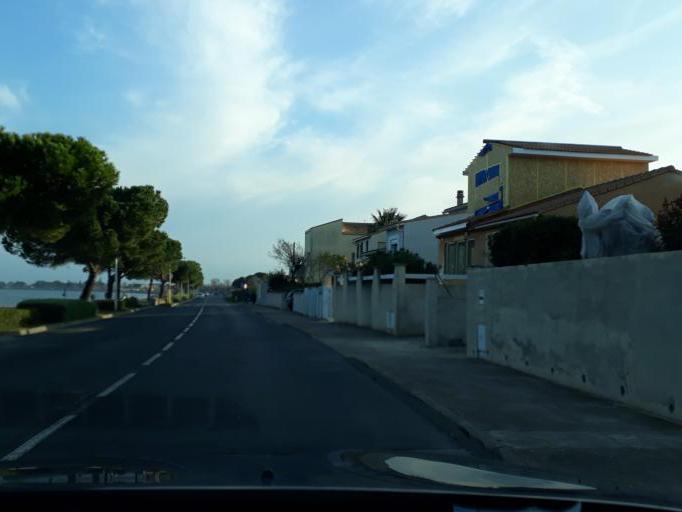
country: FR
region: Languedoc-Roussillon
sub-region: Departement de l'Herault
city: Marseillan
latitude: 43.3486
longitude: 3.5310
